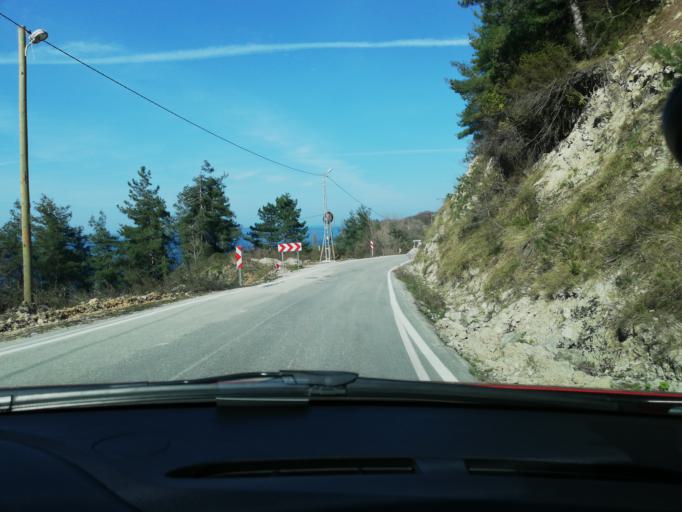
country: TR
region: Bartin
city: Kurucasile
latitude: 41.8362
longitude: 32.7094
